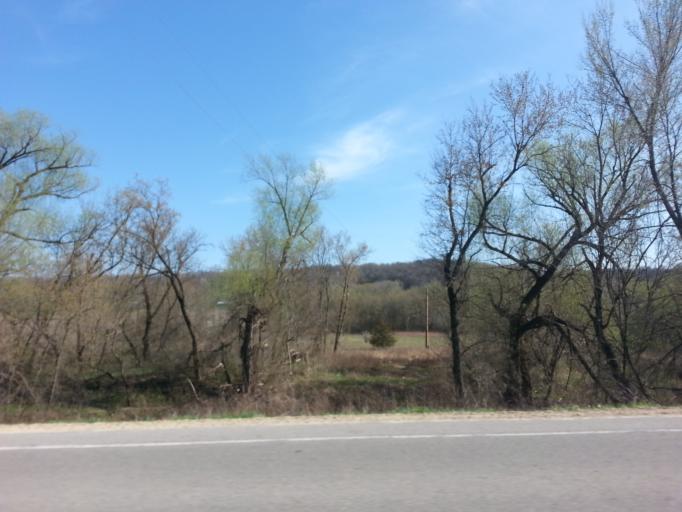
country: US
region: Wisconsin
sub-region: Pierce County
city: Ellsworth
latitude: 44.7761
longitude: -92.5231
